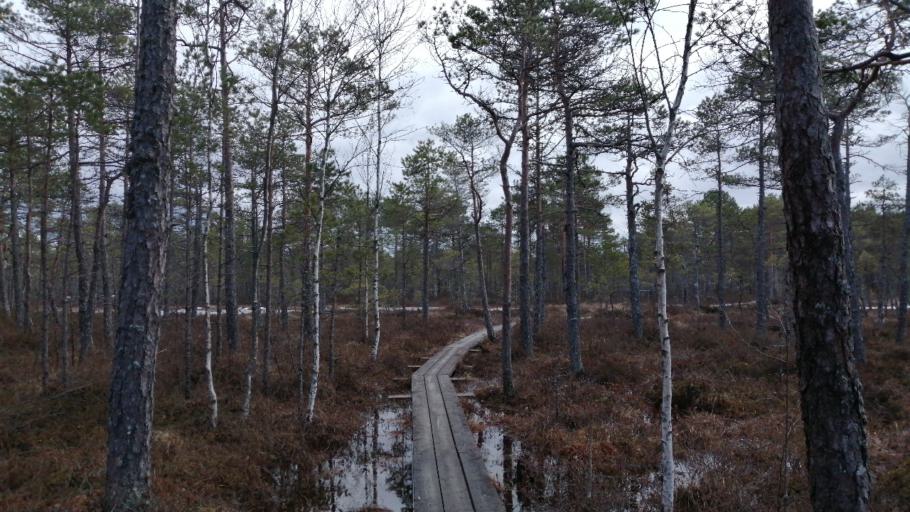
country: EE
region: Ida-Virumaa
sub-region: Kohtla-Nomme vald
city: Kohtla-Nomme
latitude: 59.1710
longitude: 27.2796
